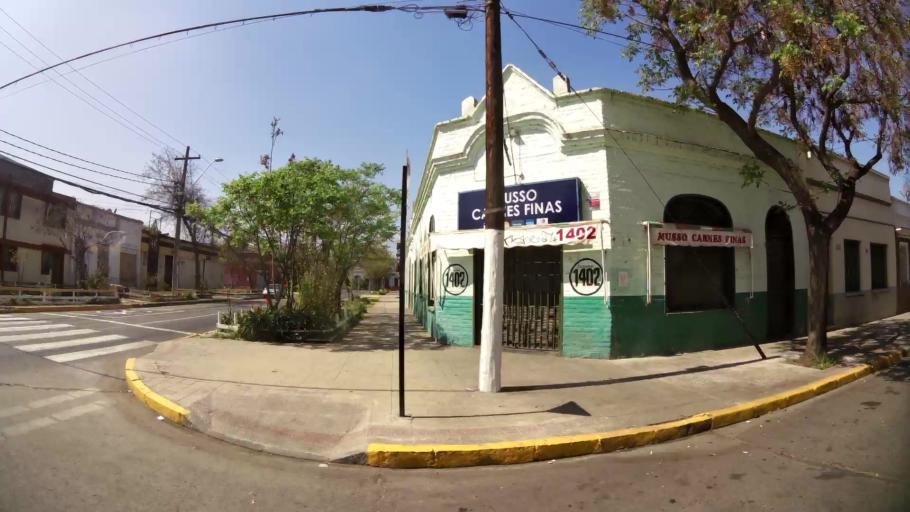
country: CL
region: Santiago Metropolitan
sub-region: Provincia de Santiago
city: Santiago
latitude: -33.4616
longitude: -70.6331
